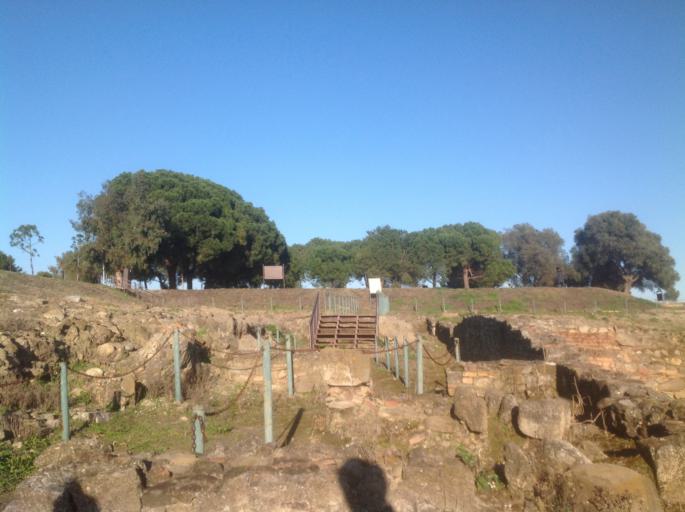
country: IT
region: Calabria
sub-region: Provincia di Cosenza
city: Sibari
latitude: 39.7161
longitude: 16.4907
